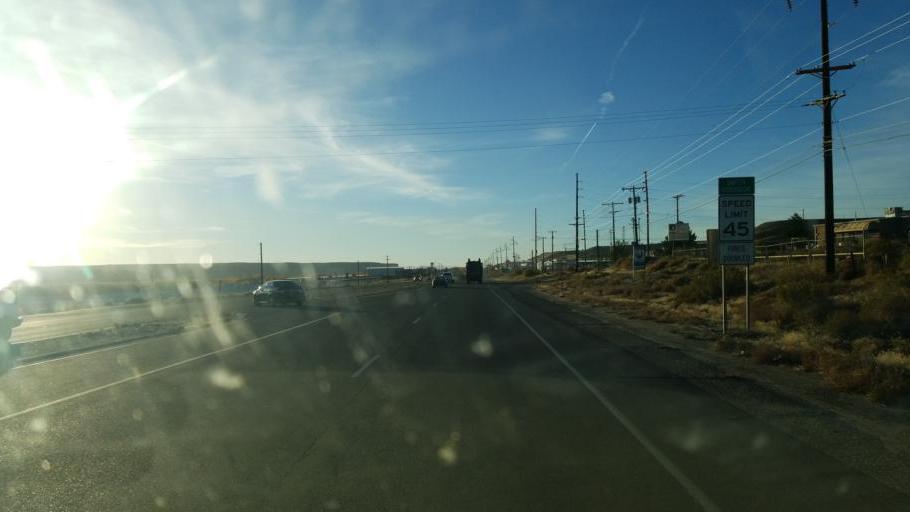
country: US
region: New Mexico
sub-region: San Juan County
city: Lee Acres
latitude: 36.7026
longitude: -108.0969
